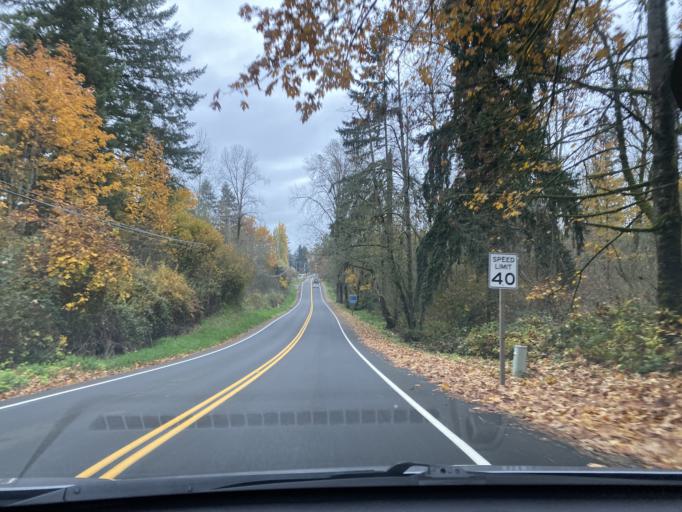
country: US
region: Washington
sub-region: King County
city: Lake Morton-Berrydale
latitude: 47.3006
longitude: -122.1365
